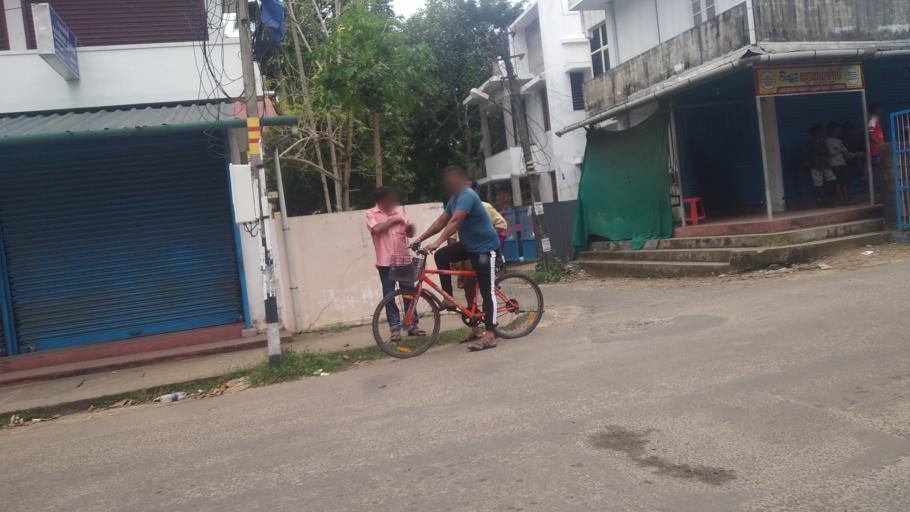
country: IN
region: Kerala
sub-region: Alappuzha
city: Arukutti
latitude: 9.8734
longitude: 76.2895
